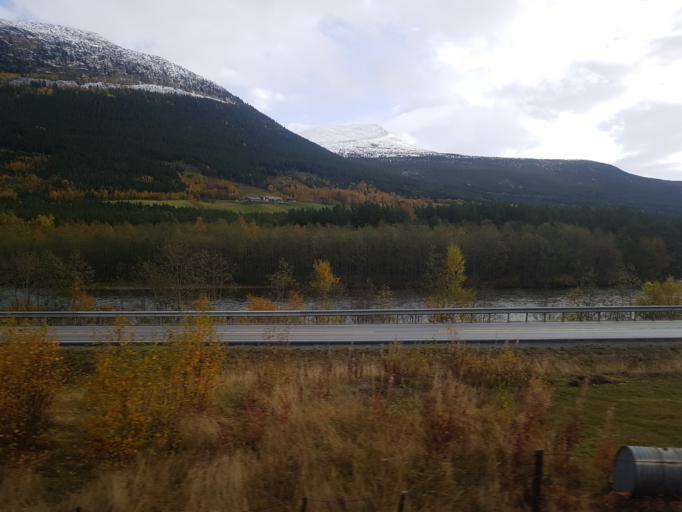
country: NO
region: Oppland
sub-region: Dovre
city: Dovre
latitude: 61.9306
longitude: 9.3208
